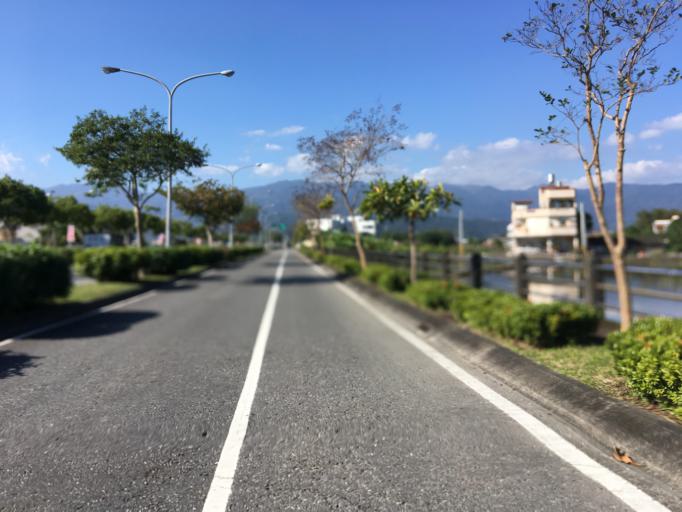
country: TW
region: Taiwan
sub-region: Yilan
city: Yilan
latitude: 24.7707
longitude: 121.7677
